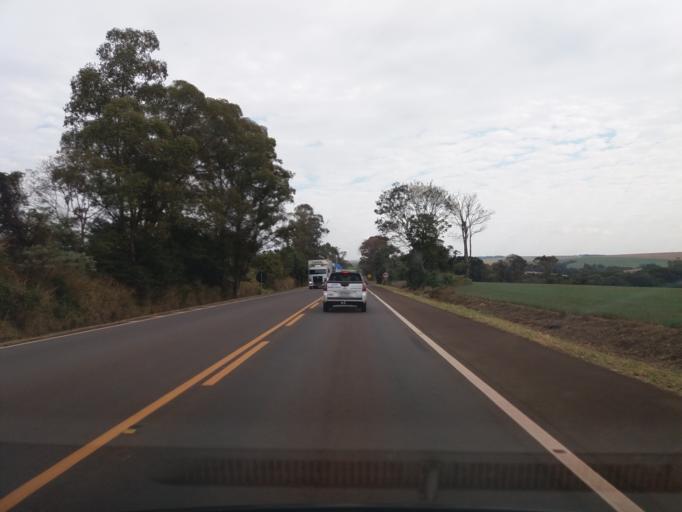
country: BR
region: Parana
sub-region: Campo Mourao
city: Campo Mourao
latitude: -24.3165
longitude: -52.6221
